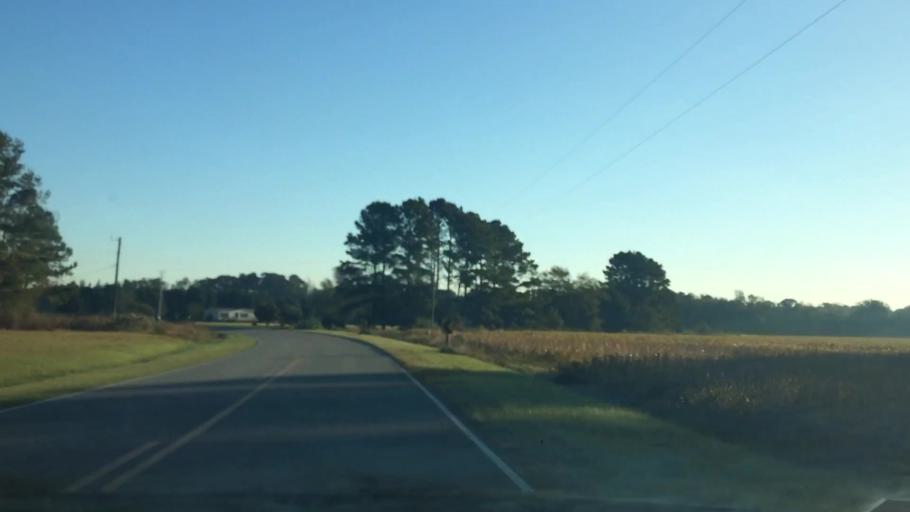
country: US
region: North Carolina
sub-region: Pitt County
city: Grifton
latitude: 35.3894
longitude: -77.4022
